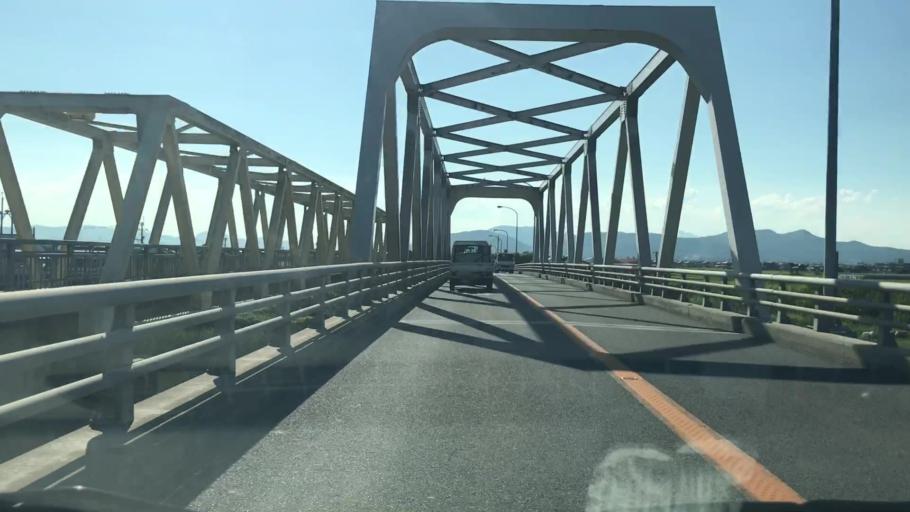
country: JP
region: Saga Prefecture
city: Saga-shi
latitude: 33.2197
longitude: 130.2518
